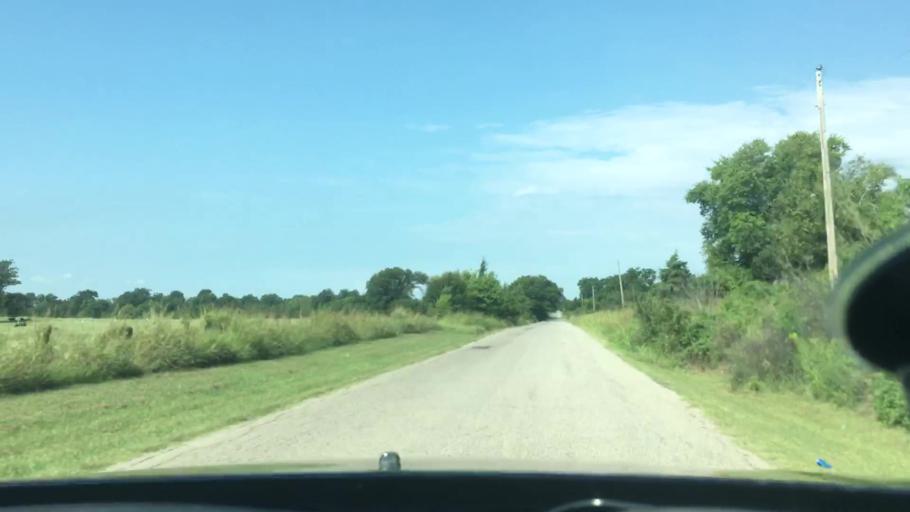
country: US
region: Oklahoma
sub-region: Bryan County
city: Calera
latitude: 33.9110
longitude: -96.4672
